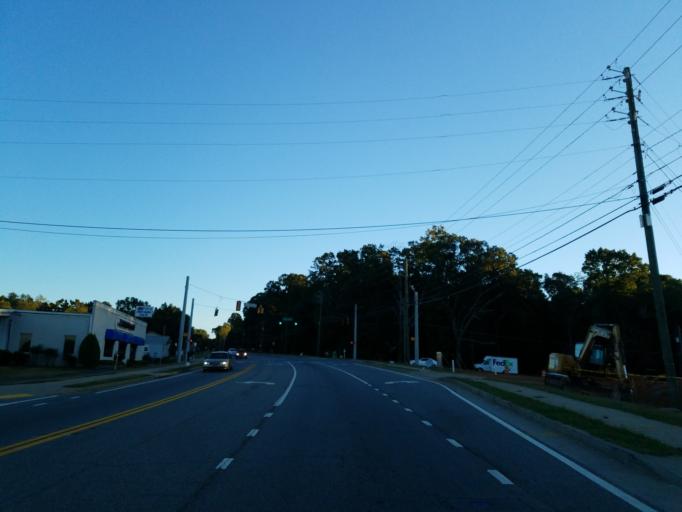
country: US
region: Georgia
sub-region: Forsyth County
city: Cumming
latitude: 34.2612
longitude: -84.1056
